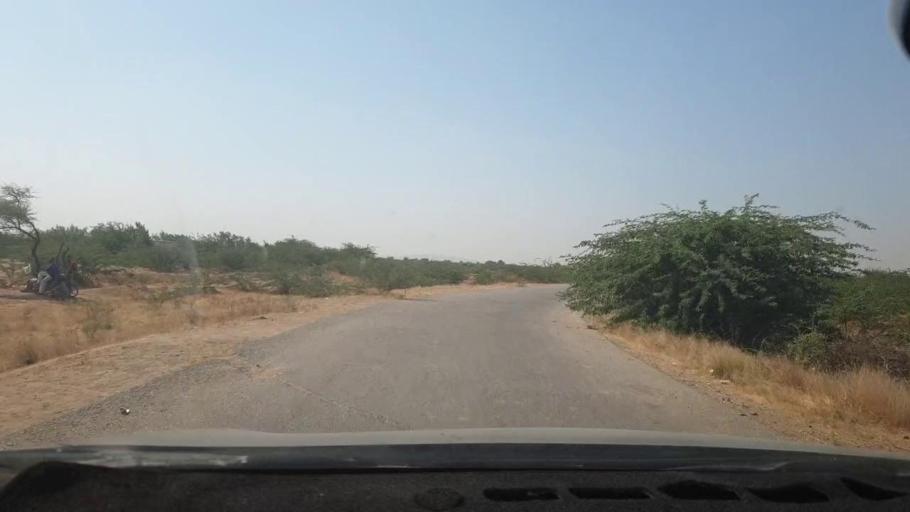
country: PK
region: Sindh
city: Malir Cantonment
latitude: 25.1562
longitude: 67.1467
